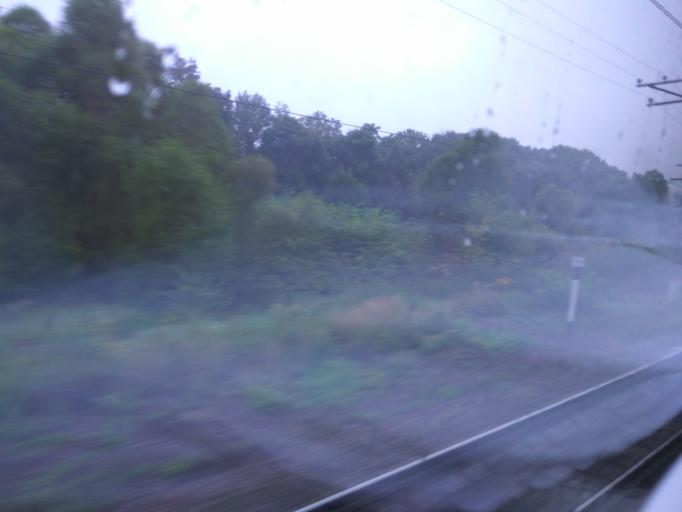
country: RU
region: Moskovskaya
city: Uzunovo
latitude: 54.5709
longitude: 38.6229
